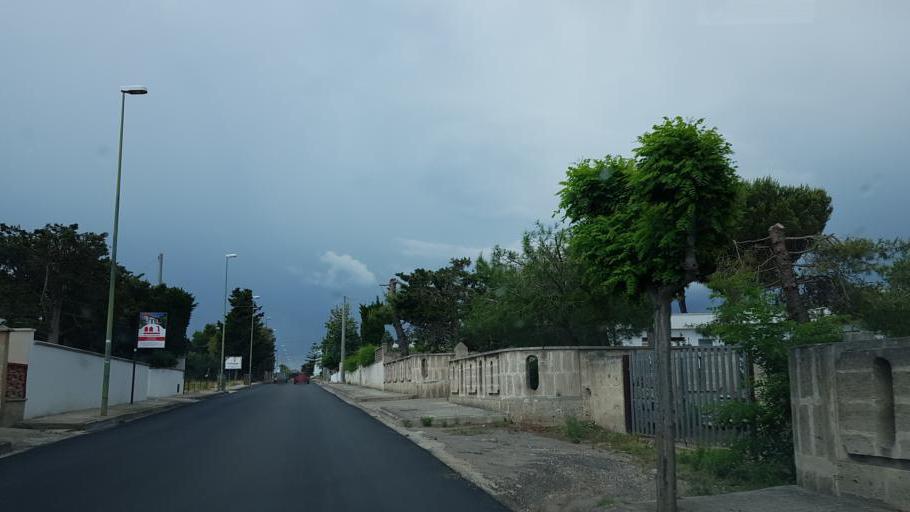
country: IT
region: Apulia
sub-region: Provincia di Lecce
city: Porto Cesareo
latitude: 40.2903
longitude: 17.8530
